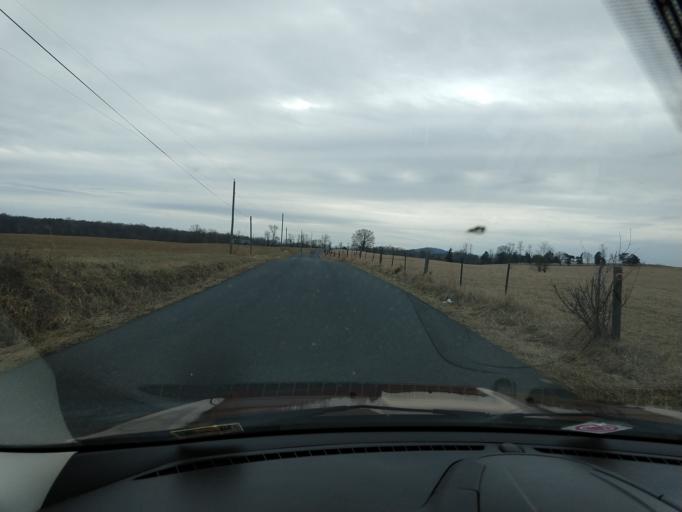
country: US
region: Virginia
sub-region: Rockingham County
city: Grottoes
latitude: 38.2429
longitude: -78.8702
